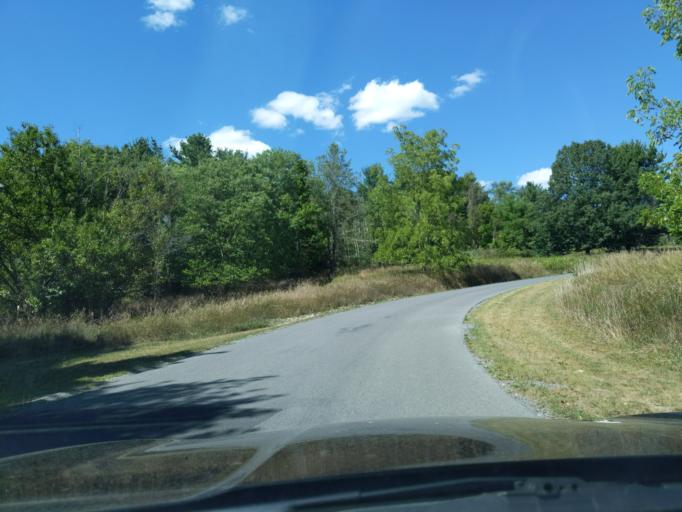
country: US
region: Pennsylvania
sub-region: Blair County
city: Greenwood
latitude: 40.4812
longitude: -78.2937
